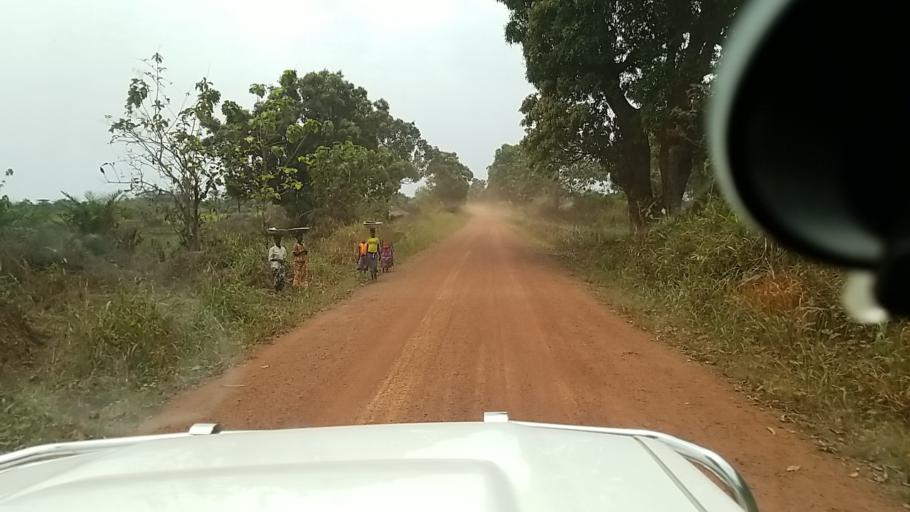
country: CD
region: Equateur
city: Libenge
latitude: 3.7358
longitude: 18.7781
